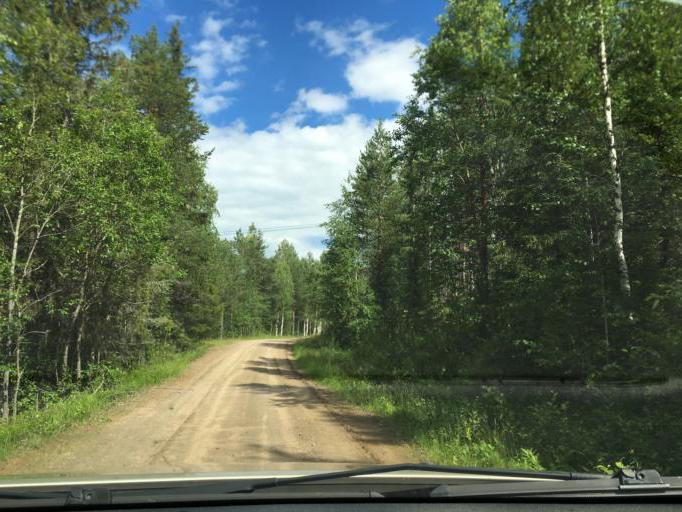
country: SE
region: Norrbotten
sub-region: Overkalix Kommun
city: OEverkalix
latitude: 66.1545
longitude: 22.7986
